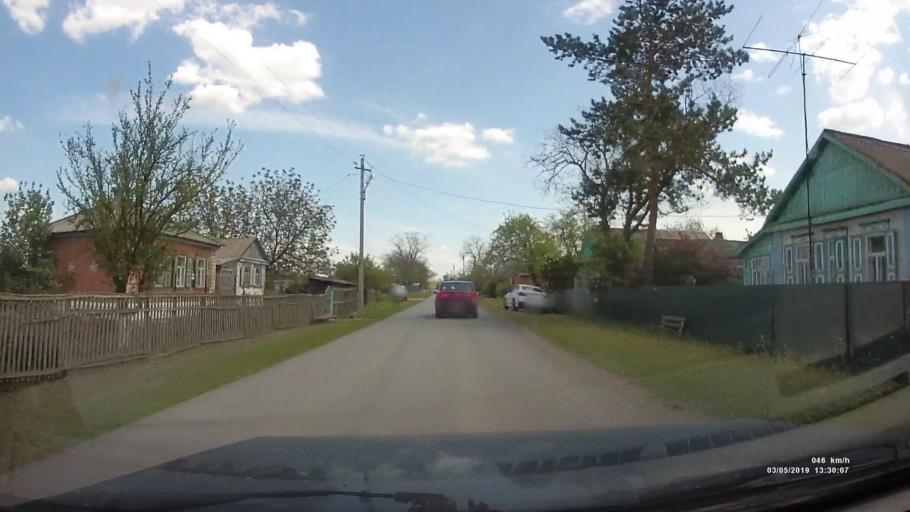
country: RU
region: Rostov
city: Ust'-Donetskiy
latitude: 47.5809
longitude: 40.8490
